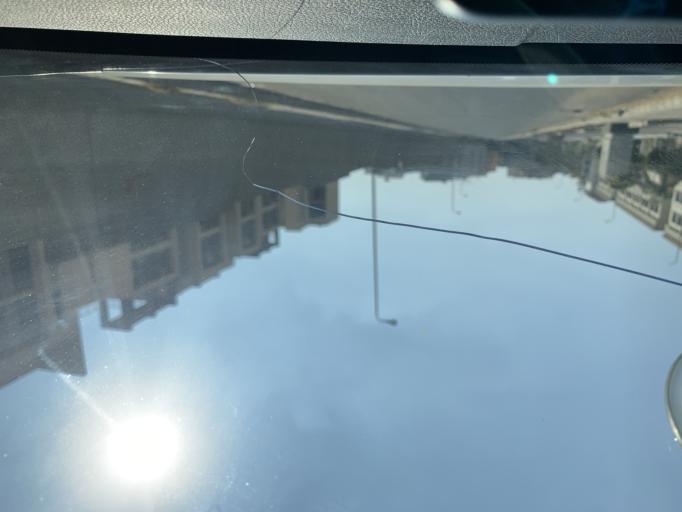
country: EG
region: Muhafazat al Qalyubiyah
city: Al Khankah
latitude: 30.0209
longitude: 31.4792
